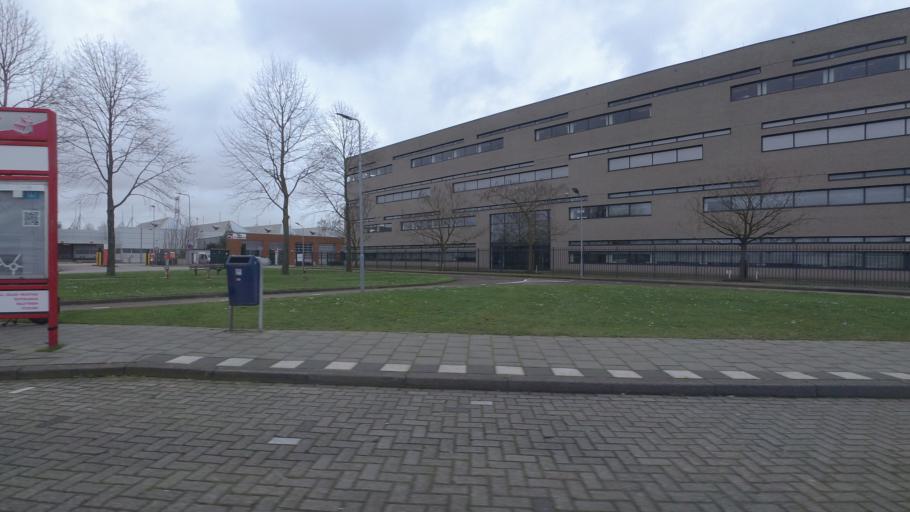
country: NL
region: North Brabant
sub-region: Gemeente Sint-Michielsgestel
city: Sint-Michielsgestel
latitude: 51.6868
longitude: 5.3583
